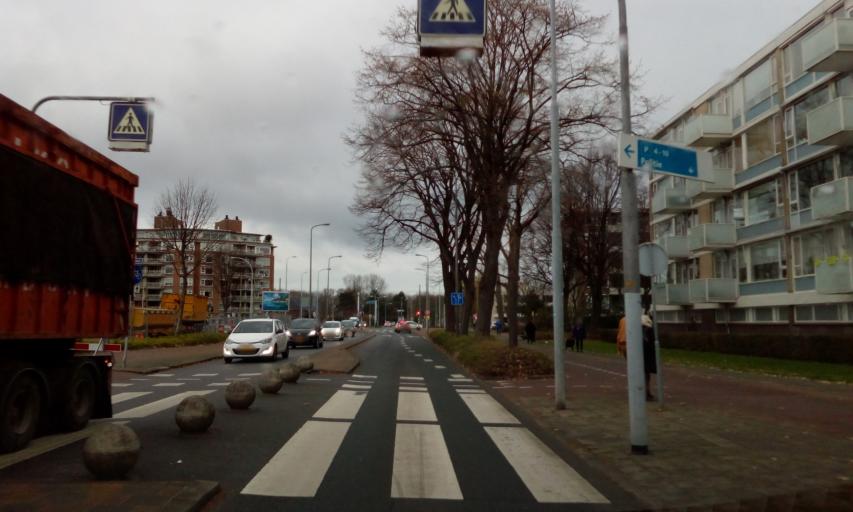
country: NL
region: South Holland
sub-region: Gemeente Leidschendam-Voorburg
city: Voorburg
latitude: 52.0907
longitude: 4.3848
